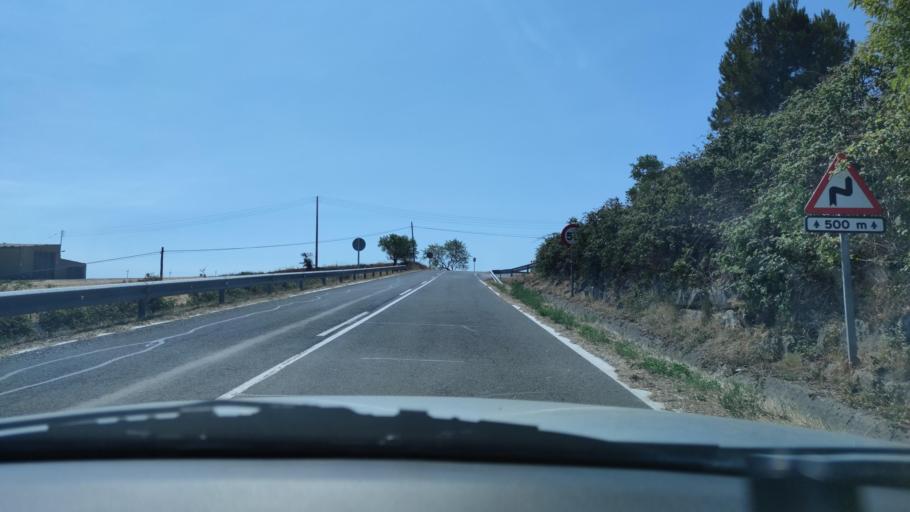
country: ES
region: Catalonia
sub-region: Provincia de Tarragona
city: Santa Coloma de Queralt
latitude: 41.5846
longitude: 1.3393
